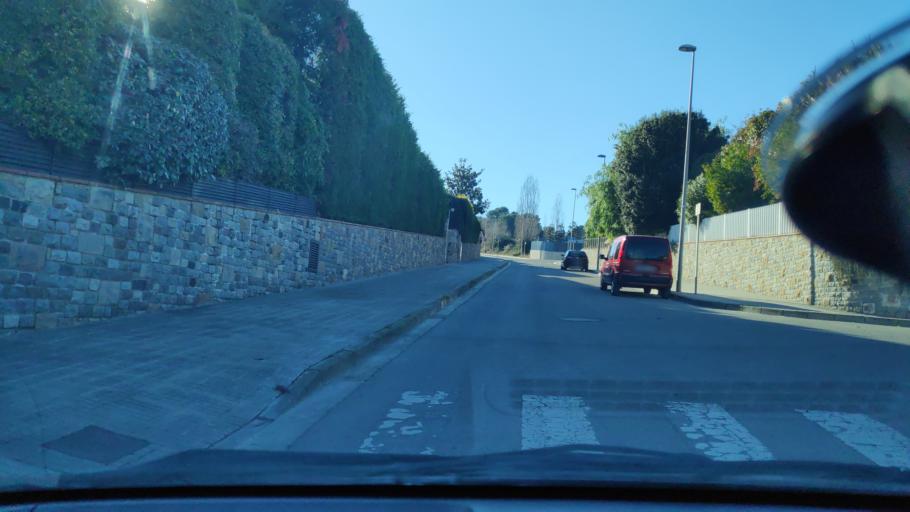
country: ES
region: Catalonia
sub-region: Provincia de Barcelona
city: Sant Quirze del Valles
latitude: 41.5354
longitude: 2.0593
